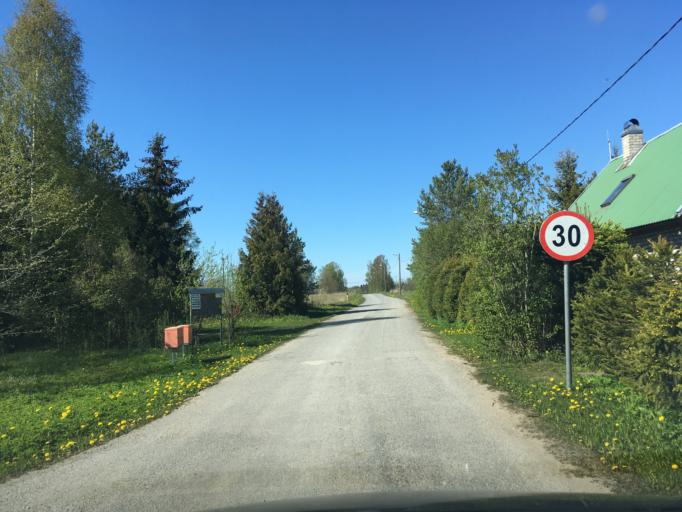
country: EE
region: Harju
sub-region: Raasiku vald
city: Arukula
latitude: 59.2645
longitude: 25.0953
